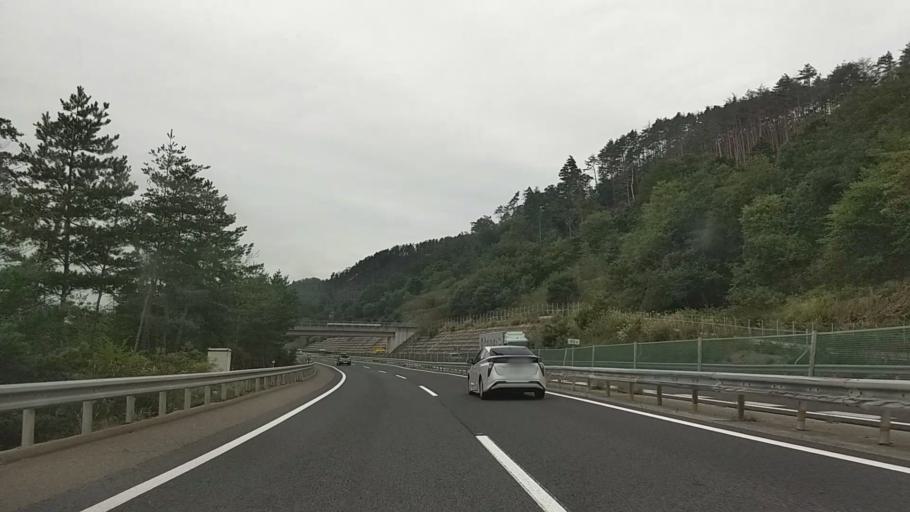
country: JP
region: Nagano
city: Hotaka
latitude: 36.4137
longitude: 138.0023
